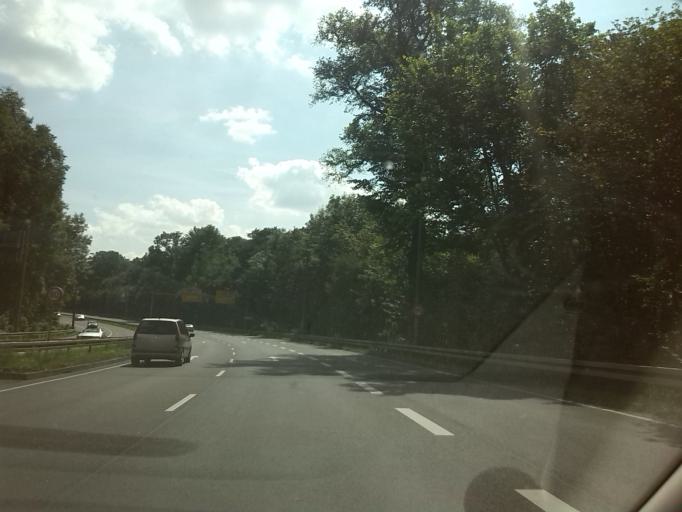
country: DE
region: Saxony
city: Leipzig
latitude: 51.3179
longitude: 12.3595
